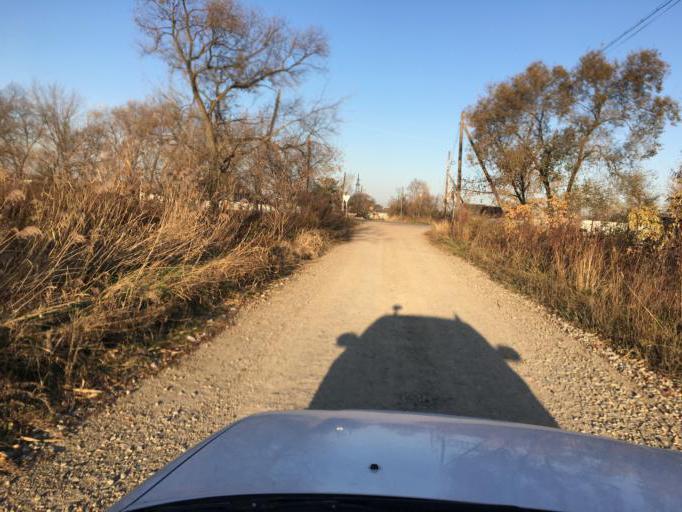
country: RU
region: Primorskiy
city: Lazo
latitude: 45.8636
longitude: 133.6427
